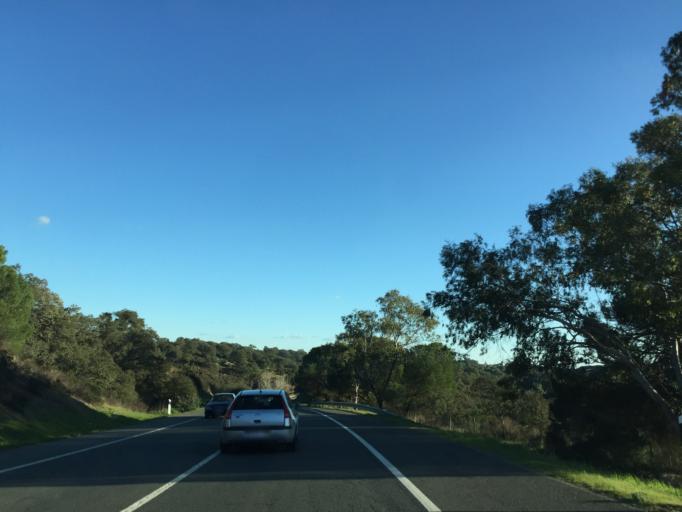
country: PT
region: Setubal
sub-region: Grandola
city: Grandola
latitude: 38.0670
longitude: -8.4129
